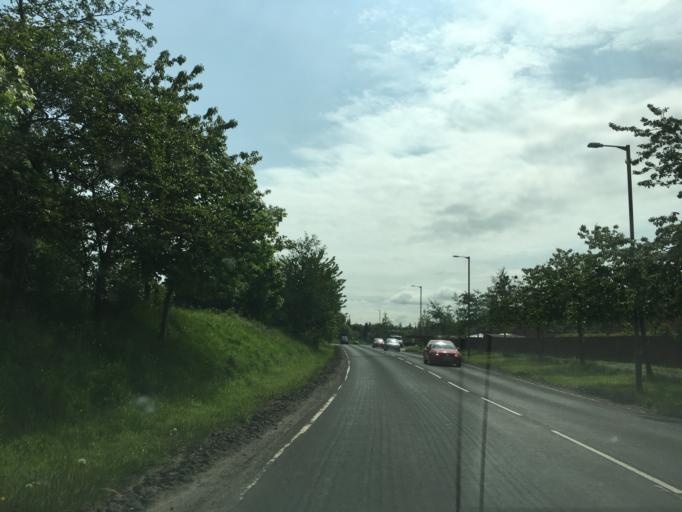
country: GB
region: Scotland
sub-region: Stirling
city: Bannockburn
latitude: 56.1017
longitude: -3.9152
